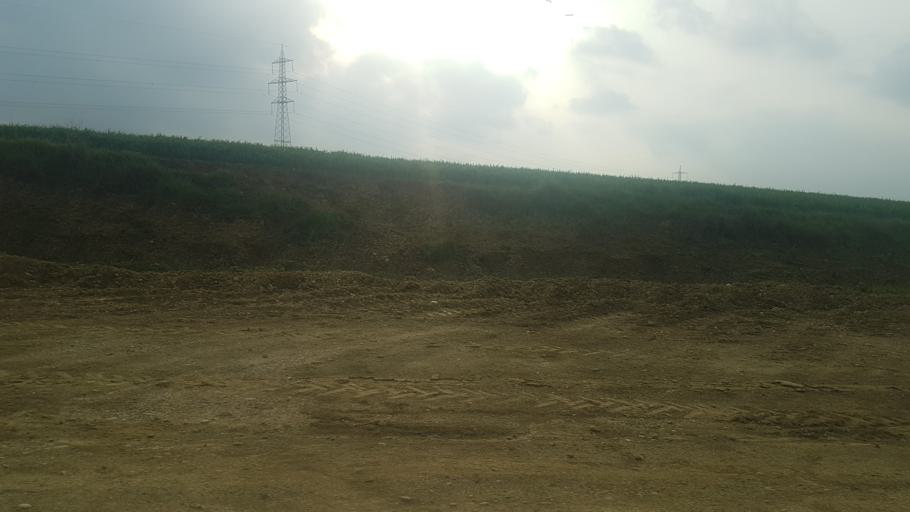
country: TR
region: Adana
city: Seyhan
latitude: 37.0470
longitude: 35.2110
